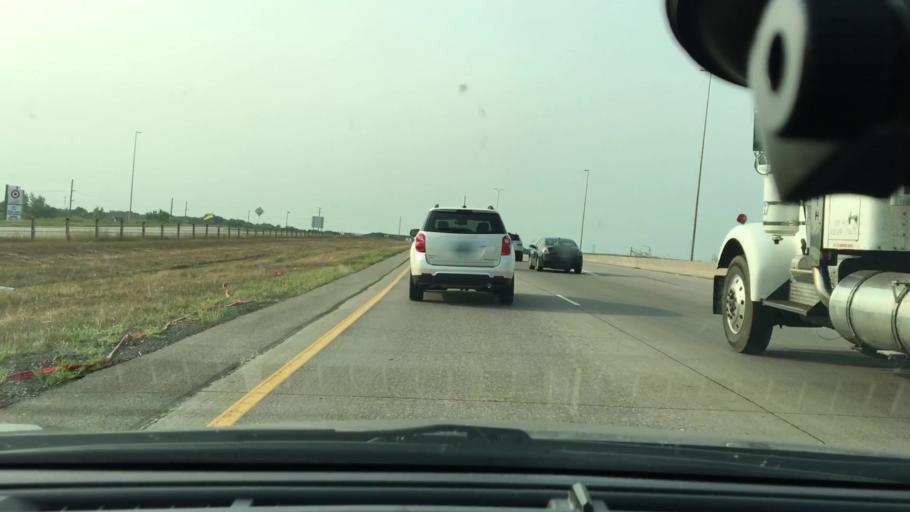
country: US
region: Minnesota
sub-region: Sherburne County
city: Elk River
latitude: 45.2772
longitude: -93.5577
